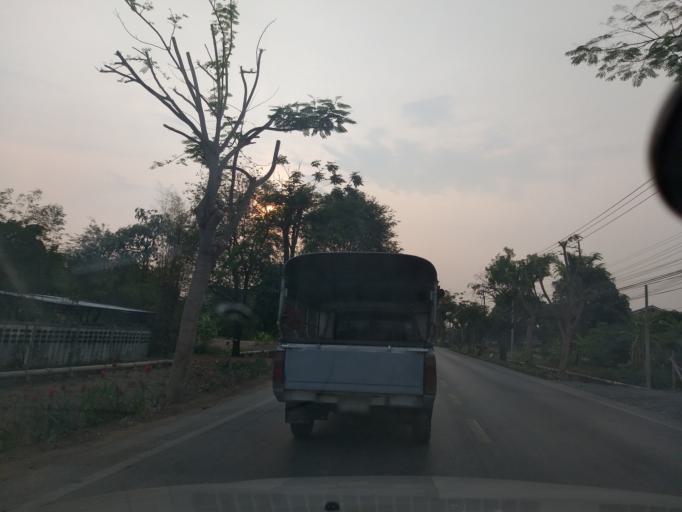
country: TH
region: Bangkok
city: Nong Chok
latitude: 13.8556
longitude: 100.8777
